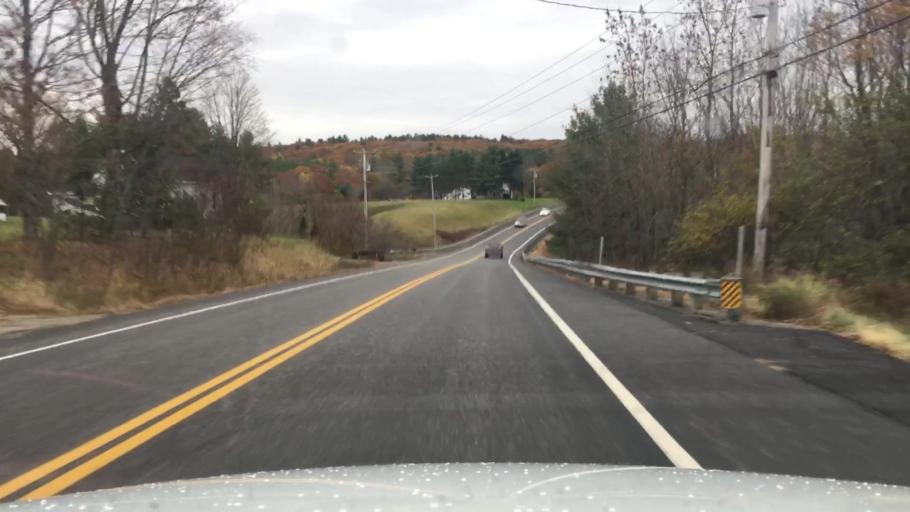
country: US
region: Maine
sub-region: Kennebec County
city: Pittston
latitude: 44.1908
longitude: -69.7472
